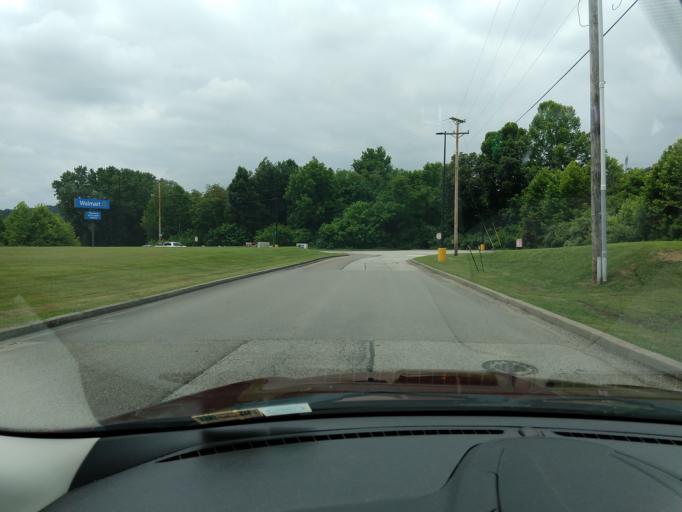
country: US
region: West Virginia
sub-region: Jackson County
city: Ripley
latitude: 38.8304
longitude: -81.7212
